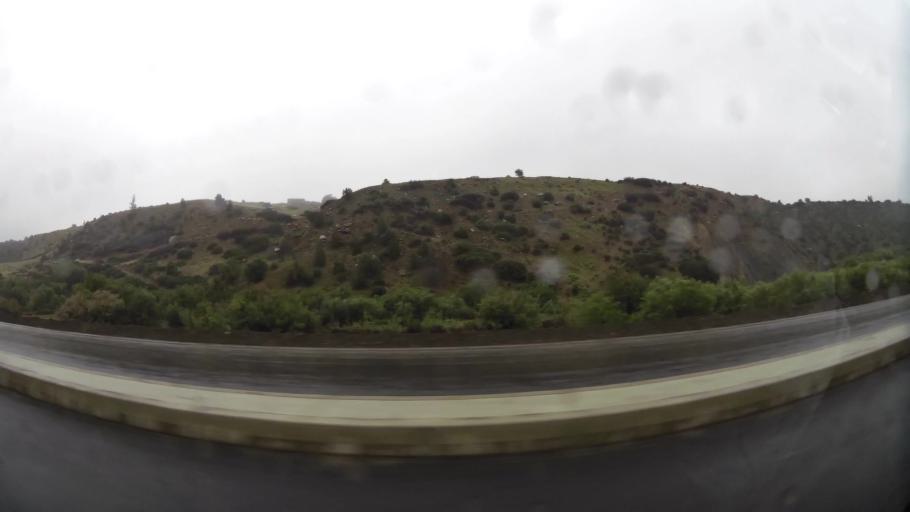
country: MA
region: Taza-Al Hoceima-Taounate
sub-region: Taza
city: Aknoul
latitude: 34.7910
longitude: -3.7546
